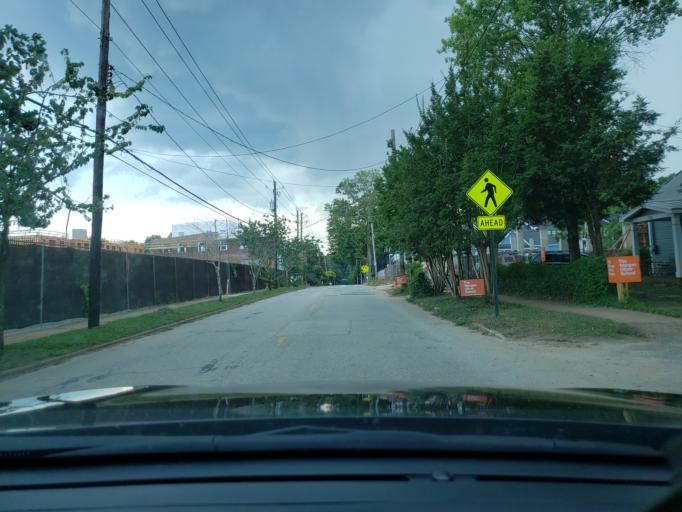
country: US
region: Georgia
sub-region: DeKalb County
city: Druid Hills
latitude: 33.7571
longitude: -84.3292
